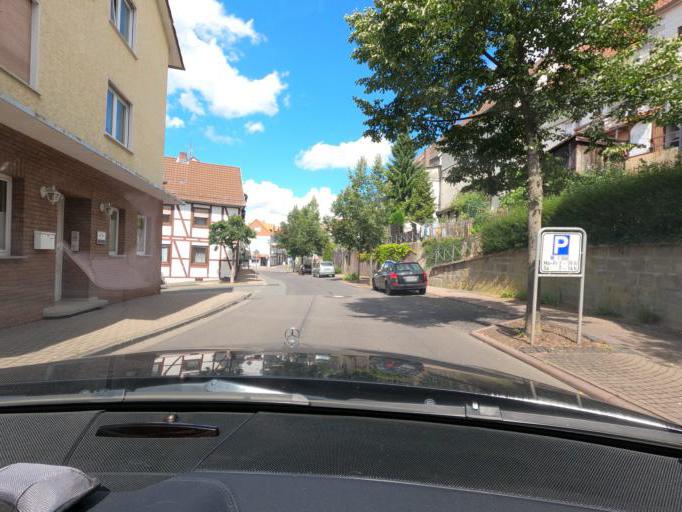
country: DE
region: Hesse
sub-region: Regierungsbezirk Kassel
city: Sontra
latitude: 51.0682
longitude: 9.9328
